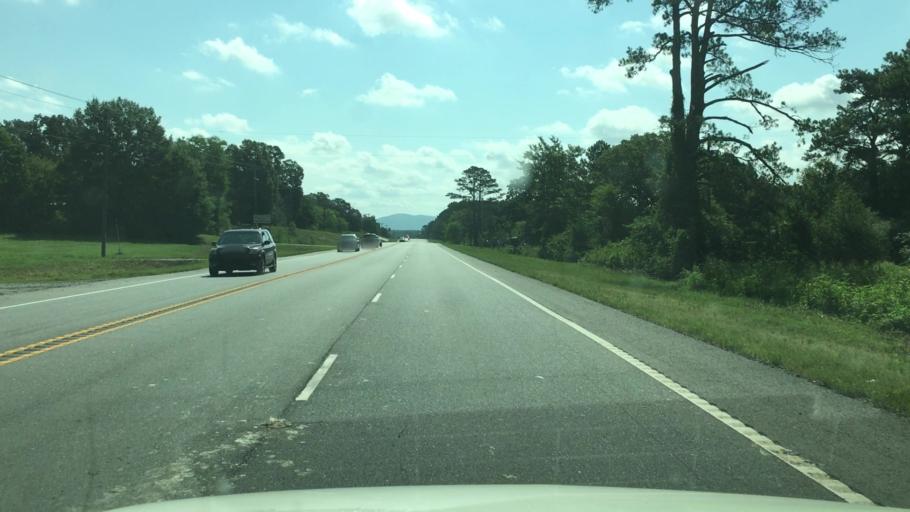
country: US
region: Arkansas
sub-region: Garland County
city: Piney
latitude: 34.5113
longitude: -93.2378
